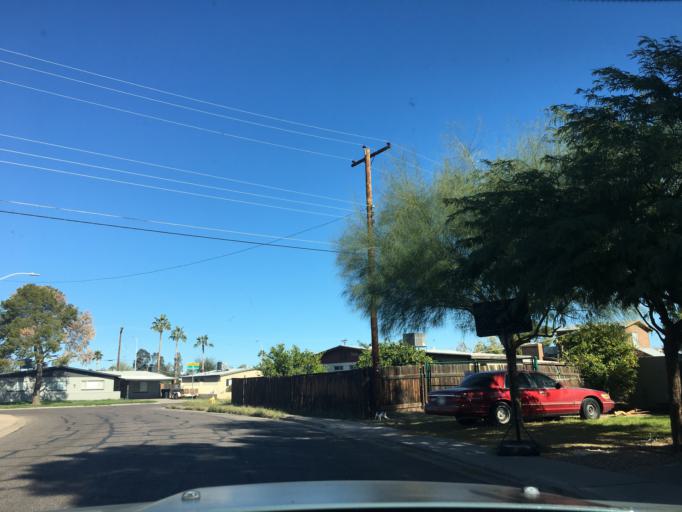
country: US
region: Arizona
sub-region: Maricopa County
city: Mesa
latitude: 33.4468
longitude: -111.8508
